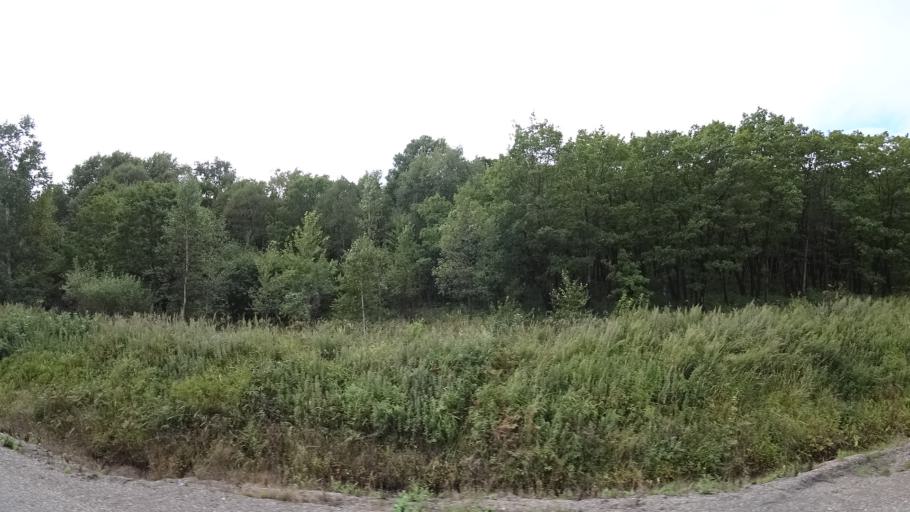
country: RU
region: Primorskiy
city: Lyalichi
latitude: 44.1057
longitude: 132.4220
